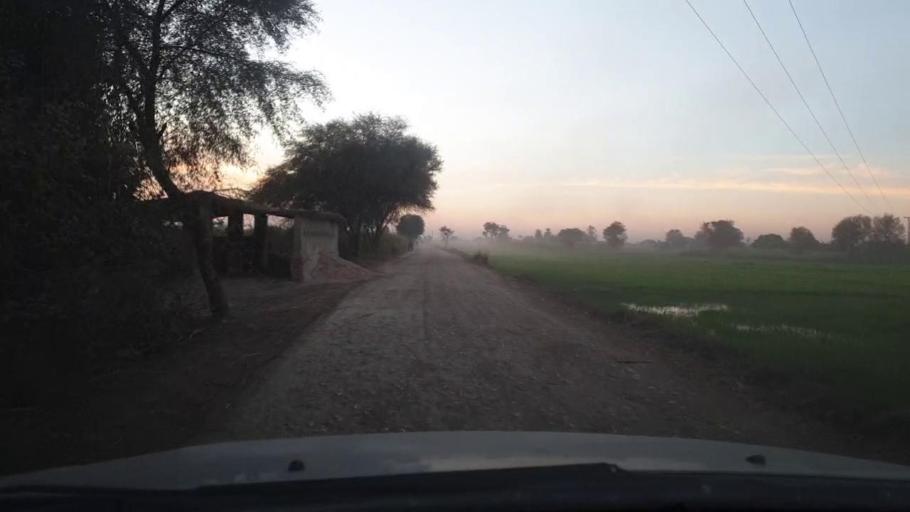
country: PK
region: Sindh
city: Ghotki
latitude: 27.9825
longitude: 69.2784
